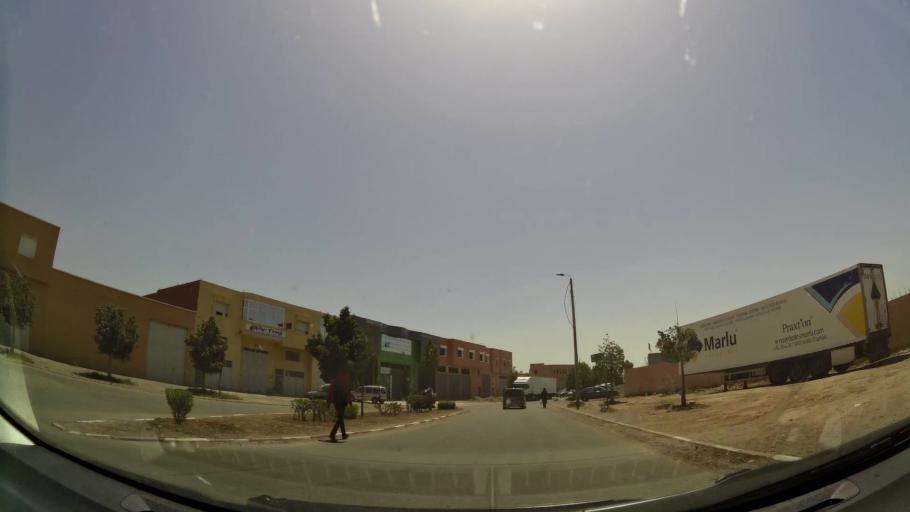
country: MA
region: Souss-Massa-Draa
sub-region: Inezgane-Ait Mellou
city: Inezgane
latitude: 30.3392
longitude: -9.4843
